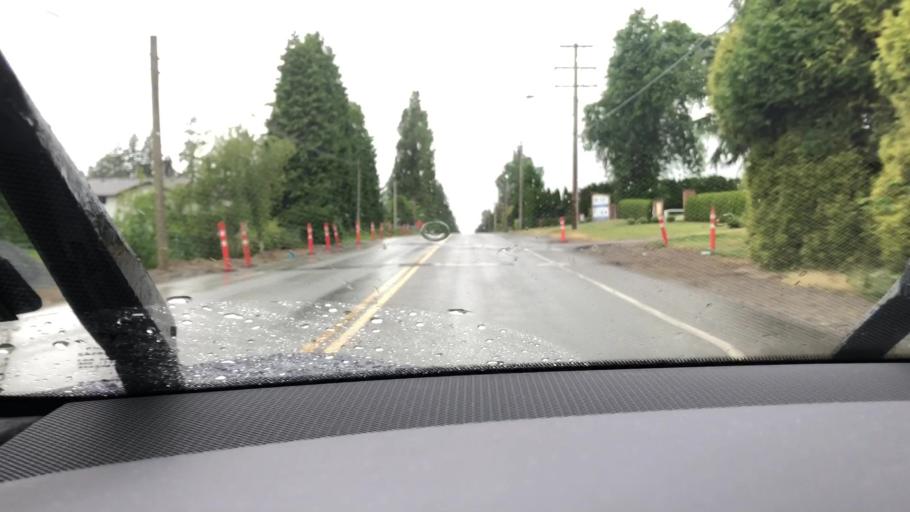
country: CA
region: British Columbia
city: Langley
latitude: 49.1334
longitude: -122.6527
